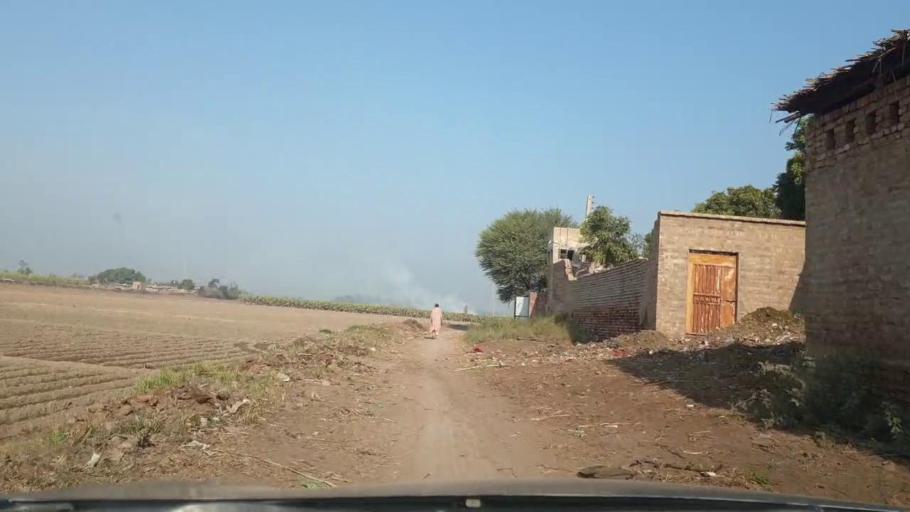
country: PK
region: Sindh
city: Tando Allahyar
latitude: 25.4869
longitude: 68.7422
